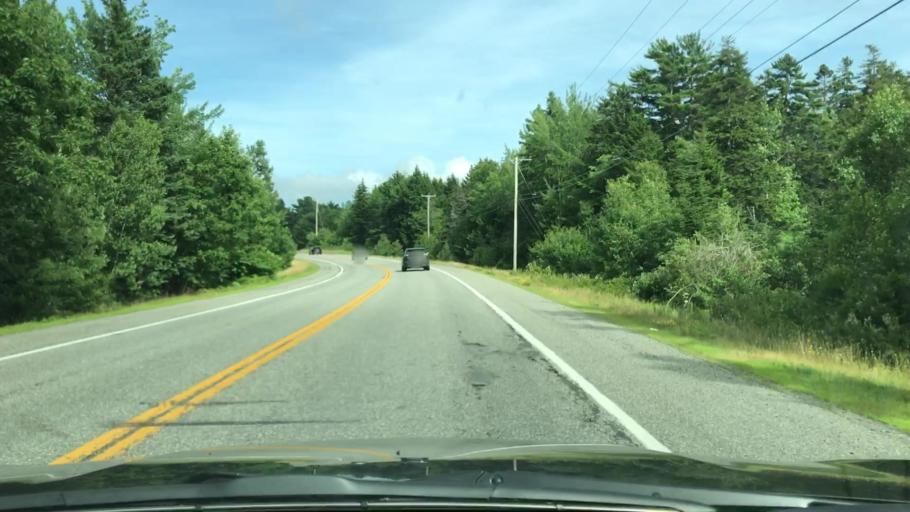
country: US
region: Maine
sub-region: Hancock County
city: Trenton
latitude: 44.4188
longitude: -68.3447
